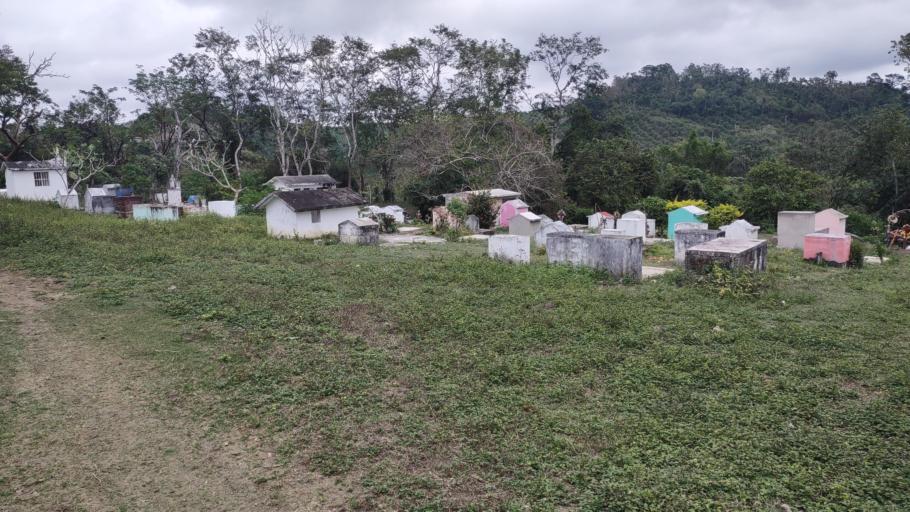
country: MX
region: Veracruz
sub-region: Coatzintla
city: Manuel Maria Contreras
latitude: 20.4104
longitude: -97.4542
